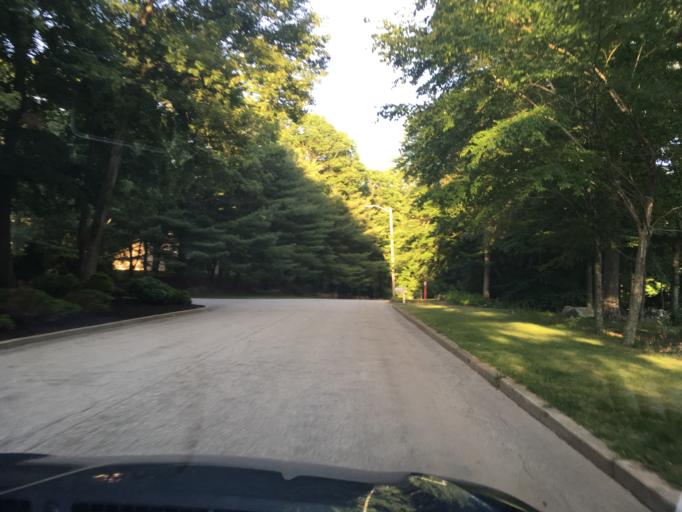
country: US
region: Rhode Island
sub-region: Washington County
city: Exeter
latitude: 41.6353
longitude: -71.5191
